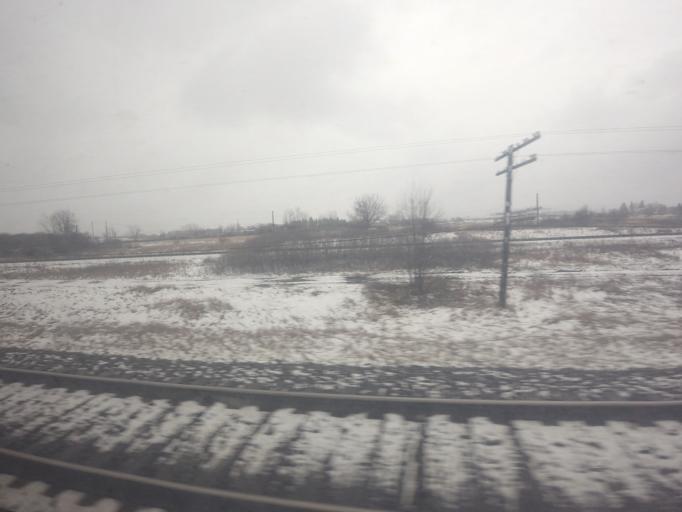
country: CA
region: Ontario
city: Quinte West
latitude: 44.0928
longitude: -77.6265
